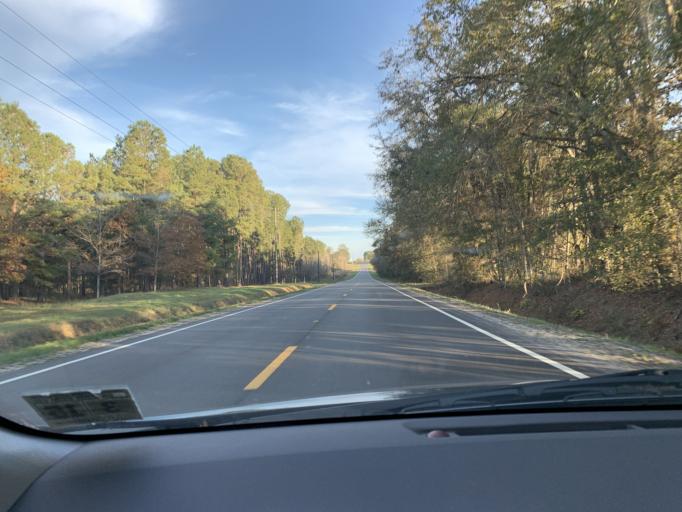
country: US
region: Georgia
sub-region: Coffee County
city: Broxton
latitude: 31.5810
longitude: -83.0632
